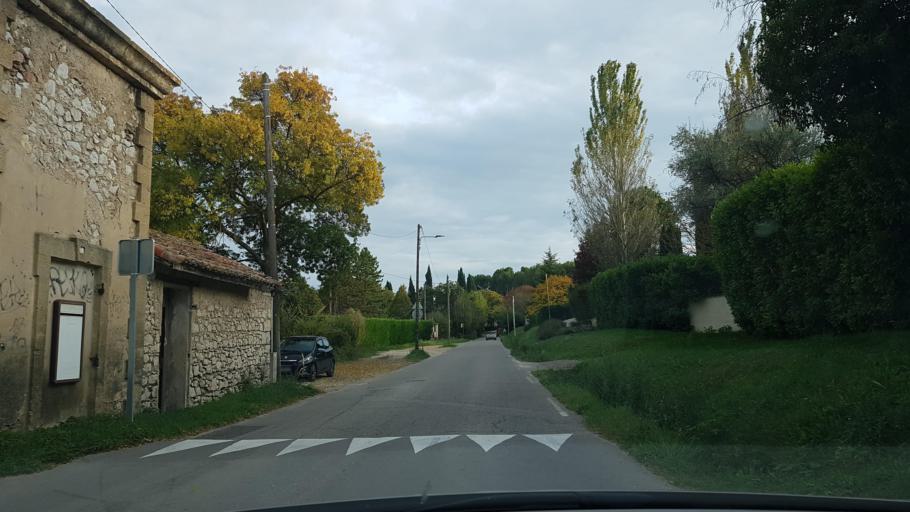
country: FR
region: Provence-Alpes-Cote d'Azur
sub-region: Departement des Bouches-du-Rhone
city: Cabries
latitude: 43.4429
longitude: 5.3748
